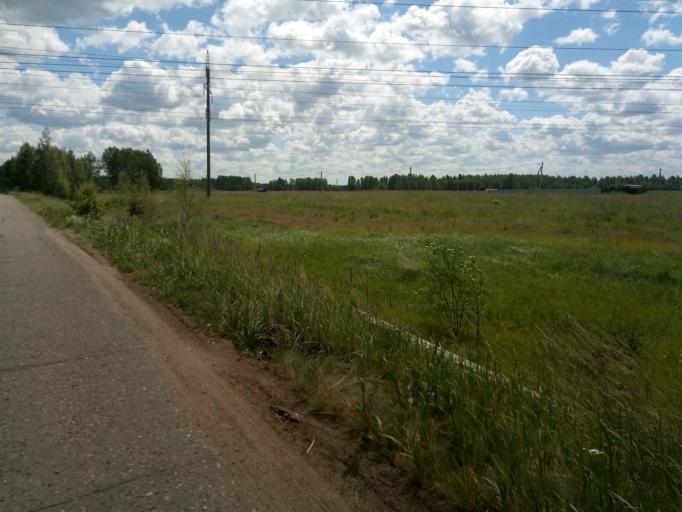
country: RU
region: Jaroslavl
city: Yaroslavl
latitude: 57.6509
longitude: 39.9937
